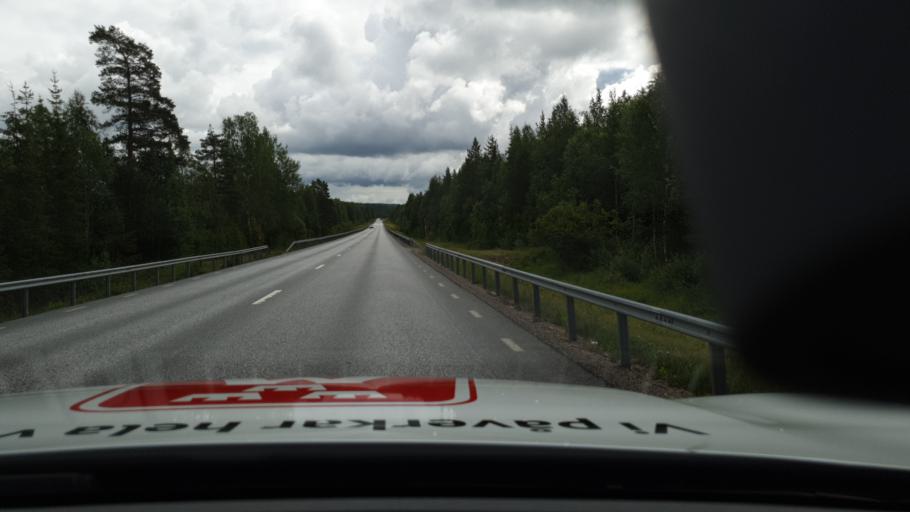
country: SE
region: Norrbotten
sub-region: Pitea Kommun
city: Norrfjarden
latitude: 65.6122
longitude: 21.4486
